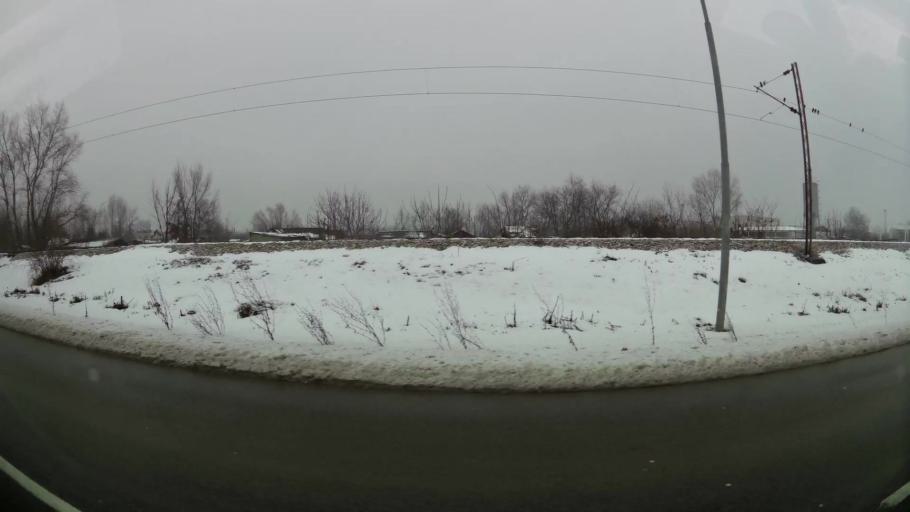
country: RS
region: Central Serbia
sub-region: Belgrade
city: Zemun
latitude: 44.8425
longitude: 20.3505
